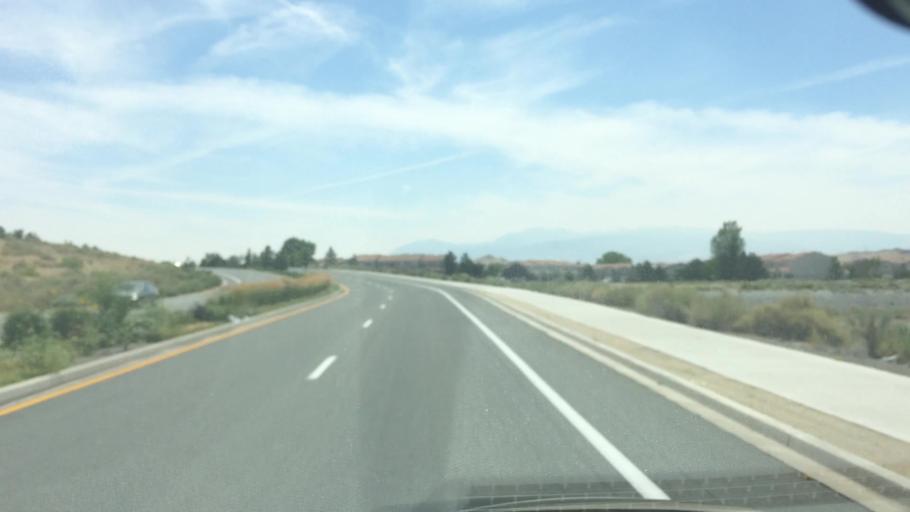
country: US
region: Nevada
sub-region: Washoe County
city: Spanish Springs
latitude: 39.5972
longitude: -119.7141
